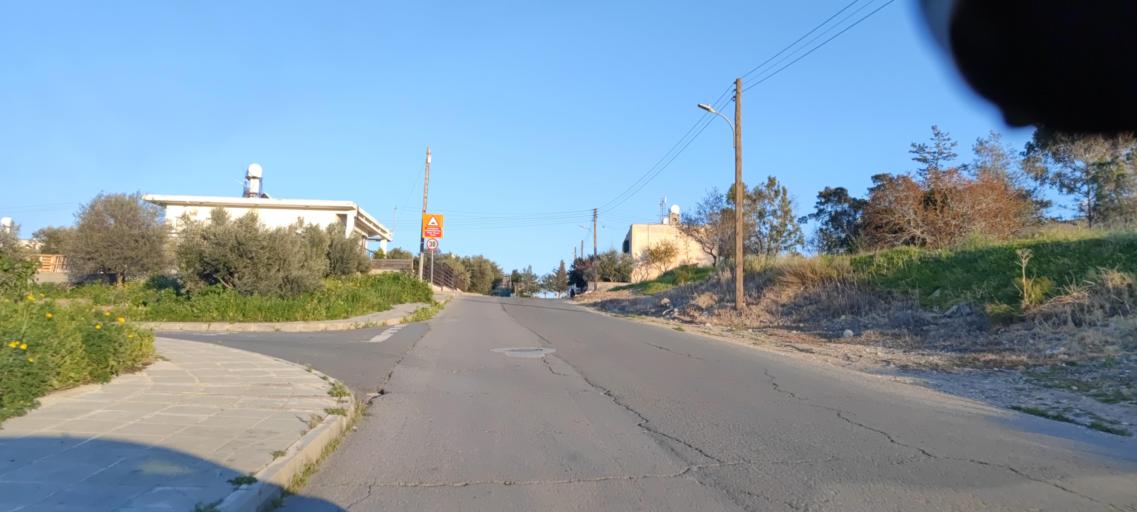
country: CY
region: Pafos
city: Paphos
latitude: 34.7839
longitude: 32.4129
